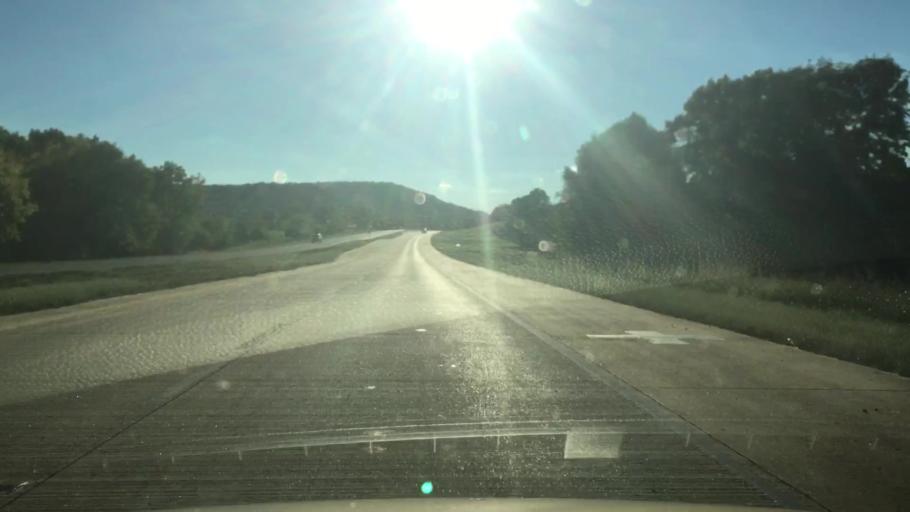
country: US
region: Oklahoma
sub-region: Cherokee County
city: Park Hill
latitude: 35.8041
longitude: -95.0839
